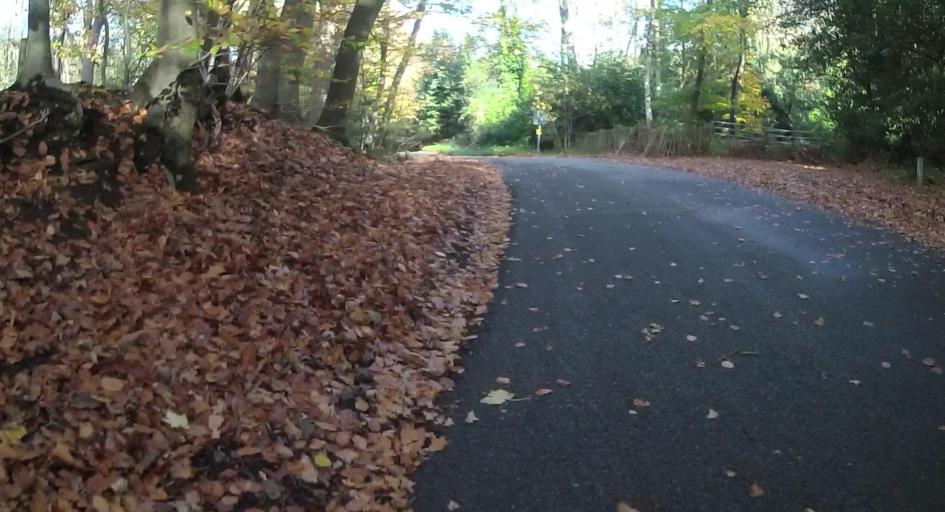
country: GB
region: England
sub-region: West Berkshire
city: Arborfield
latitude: 51.3785
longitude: -0.9275
